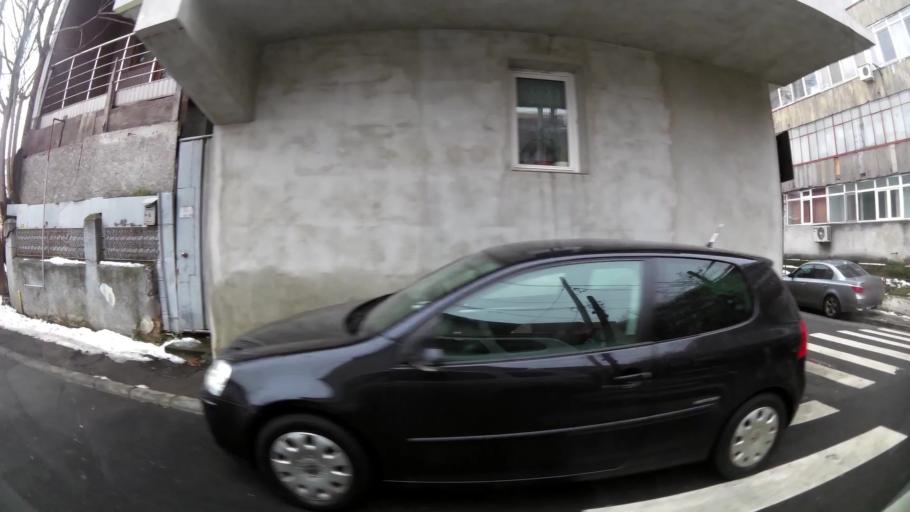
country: RO
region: Ilfov
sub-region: Comuna Chiajna
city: Rosu
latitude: 44.4591
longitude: 26.0512
